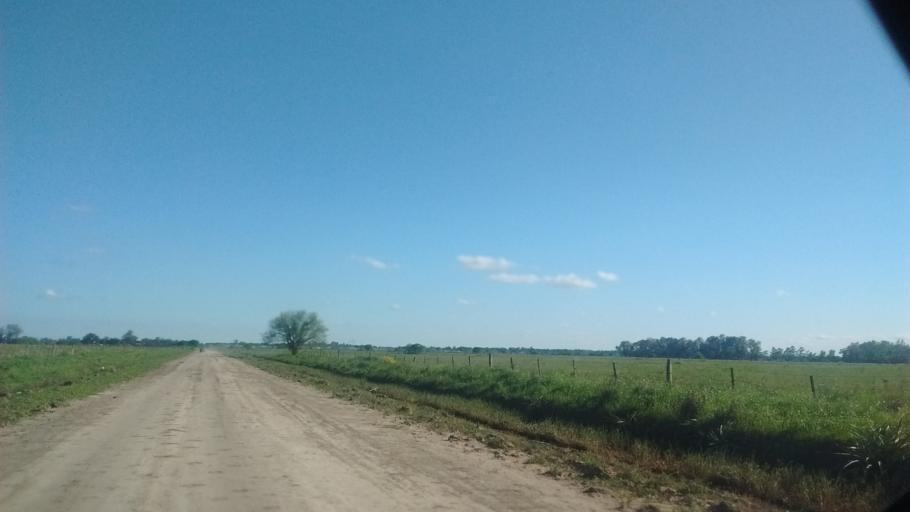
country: AR
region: Santa Fe
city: Funes
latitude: -32.8816
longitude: -60.7983
